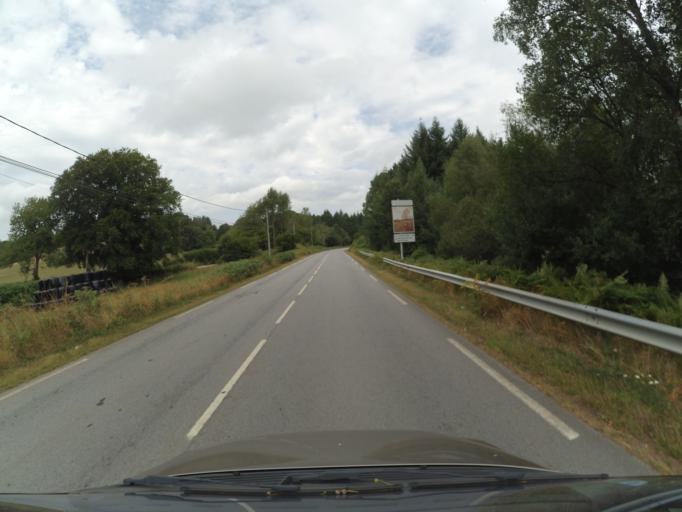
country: FR
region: Limousin
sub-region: Departement de la Correze
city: Ussel
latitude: 45.5779
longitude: 2.2937
